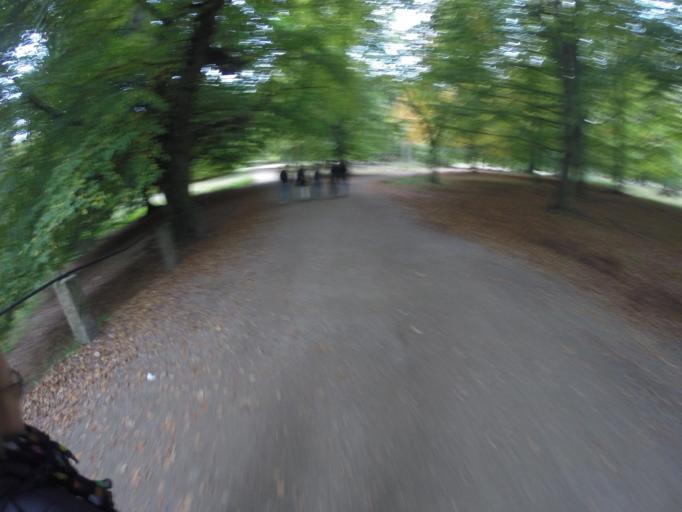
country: DK
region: Capital Region
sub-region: Gentofte Kommune
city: Charlottenlund
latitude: 55.7771
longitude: 12.5699
